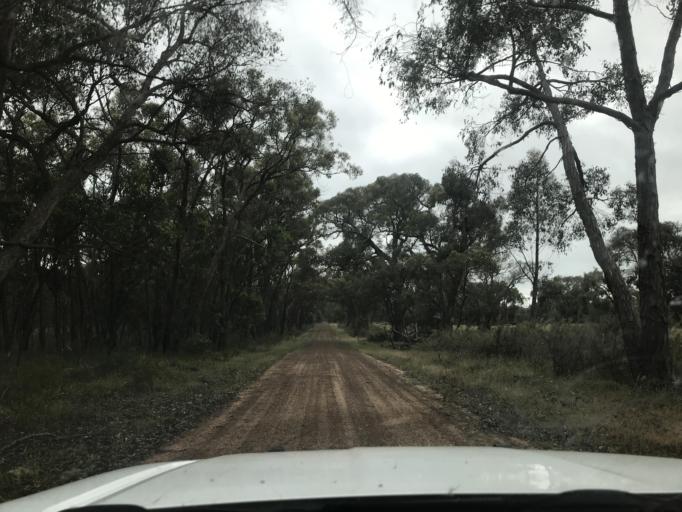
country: AU
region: South Australia
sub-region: Wattle Range
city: Penola
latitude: -37.1170
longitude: 141.1183
